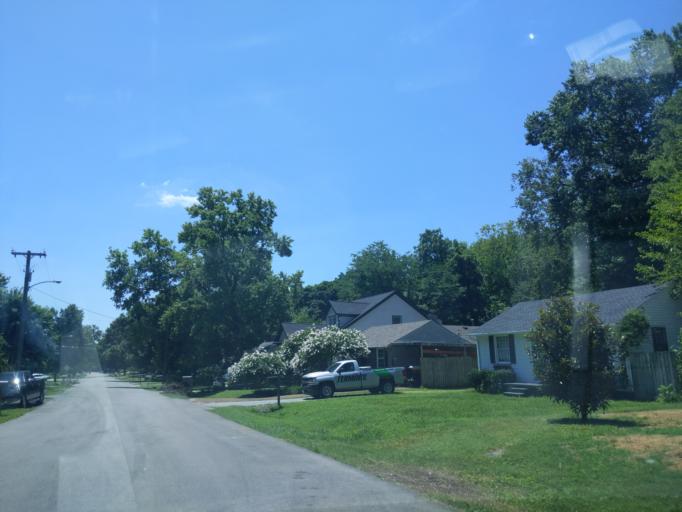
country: US
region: Tennessee
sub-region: Davidson County
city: Nashville
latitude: 36.1700
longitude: -86.7458
